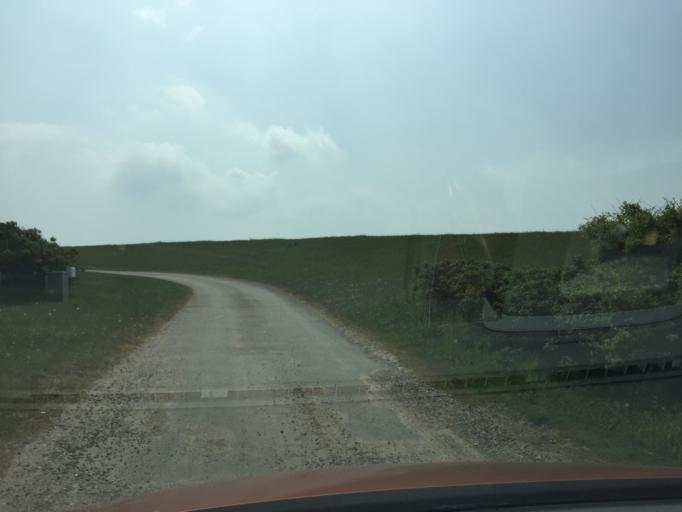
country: DK
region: South Denmark
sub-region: Esbjerg Kommune
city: Tjaereborg
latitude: 55.2687
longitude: 8.5398
